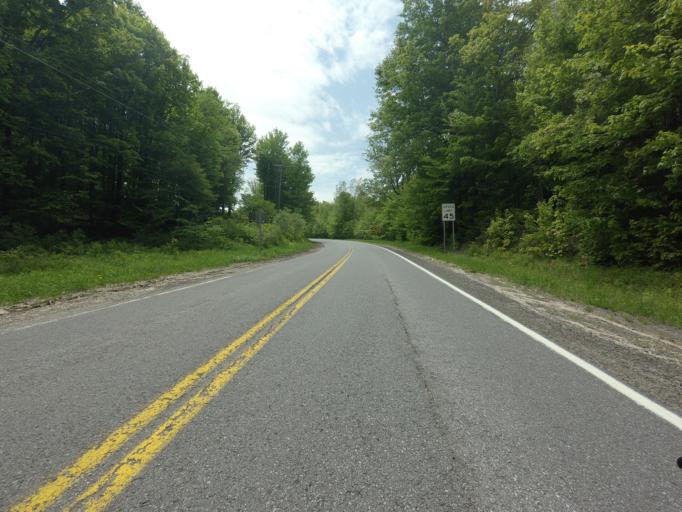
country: US
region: New York
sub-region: St. Lawrence County
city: Hannawa Falls
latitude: 44.5480
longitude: -75.0052
